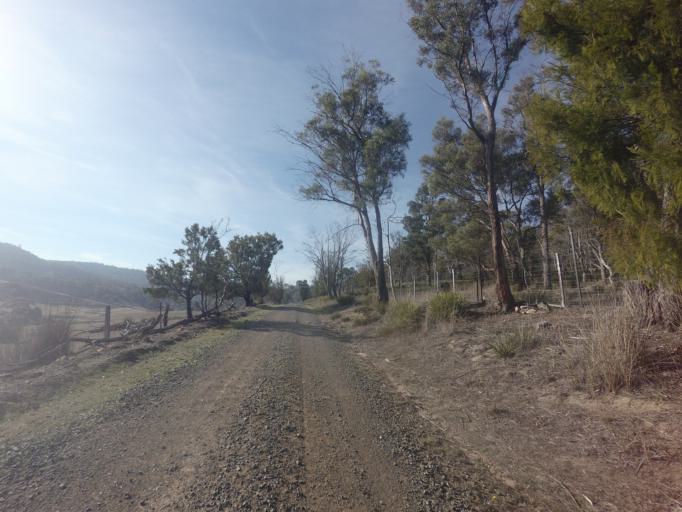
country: AU
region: Tasmania
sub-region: Sorell
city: Sorell
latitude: -42.5353
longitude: 147.4354
